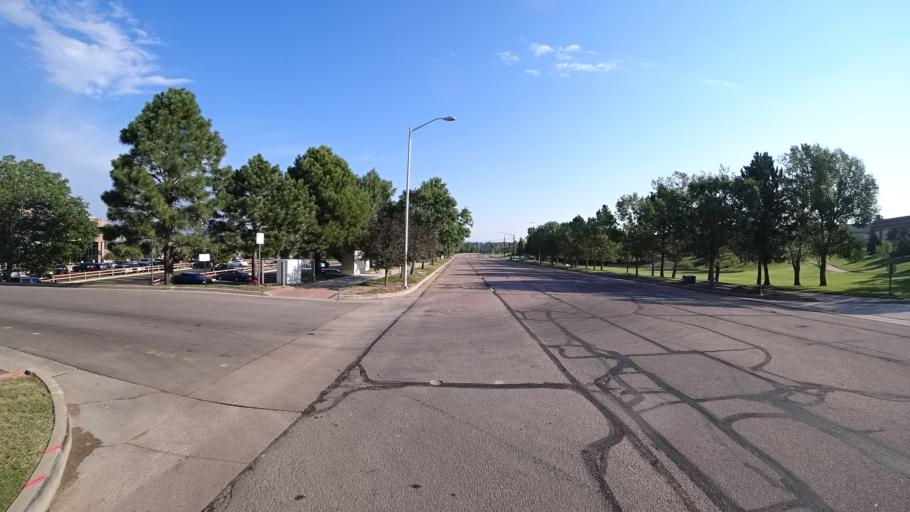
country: US
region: Colorado
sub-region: El Paso County
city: Air Force Academy
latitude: 38.9609
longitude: -104.7918
